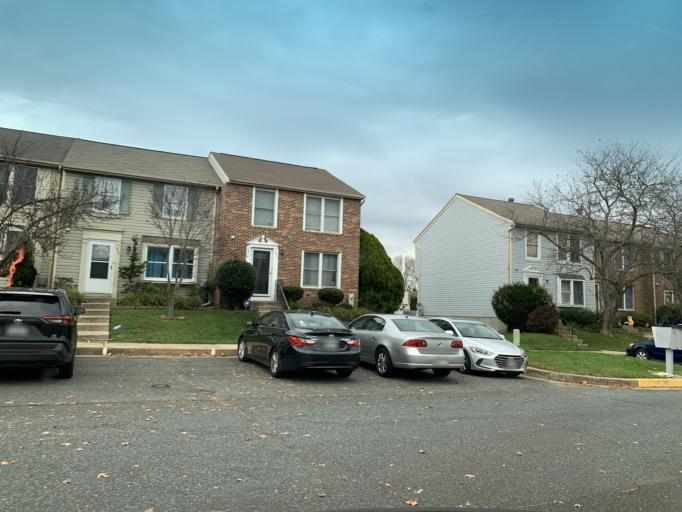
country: US
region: Maryland
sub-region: Harford County
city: Bel Air
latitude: 39.5486
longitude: -76.3446
